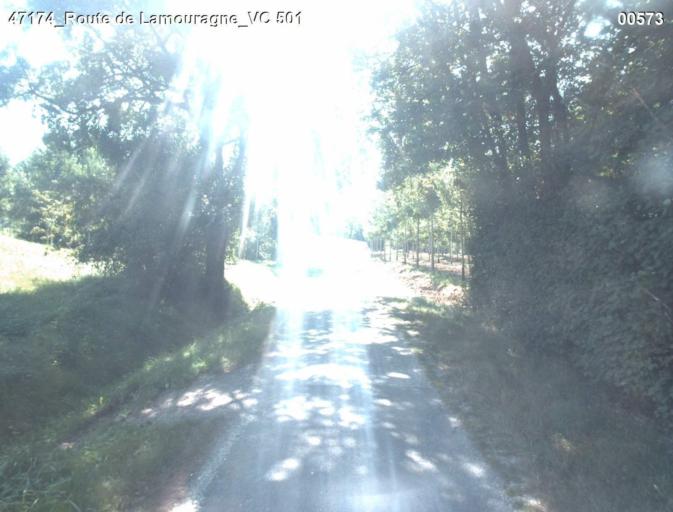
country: FR
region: Midi-Pyrenees
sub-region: Departement du Gers
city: Condom
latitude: 44.0425
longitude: 0.3859
